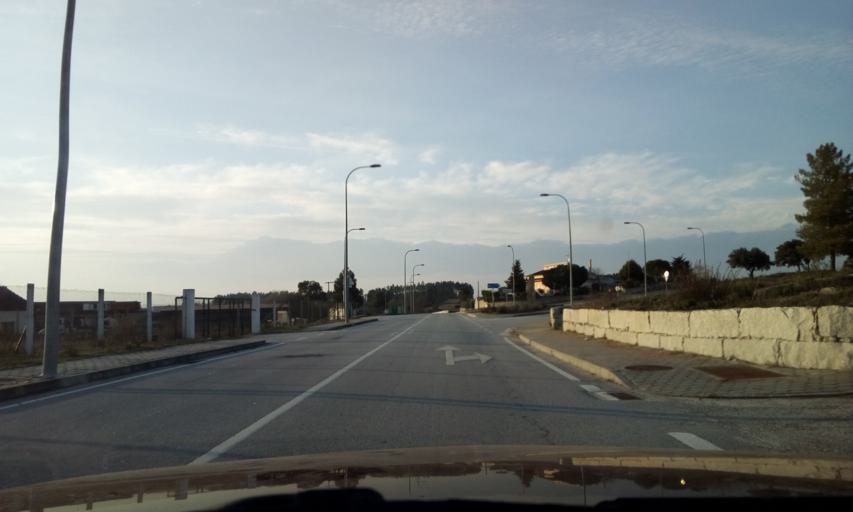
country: PT
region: Guarda
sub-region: Pinhel
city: Pinhel
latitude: 40.6027
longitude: -7.0014
